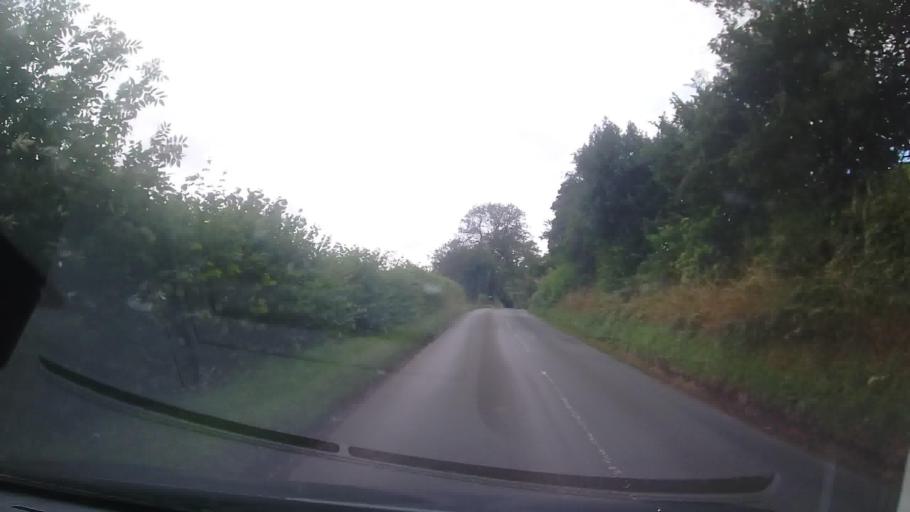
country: GB
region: England
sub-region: Shropshire
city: Pontesbury
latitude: 52.5752
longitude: -2.8867
